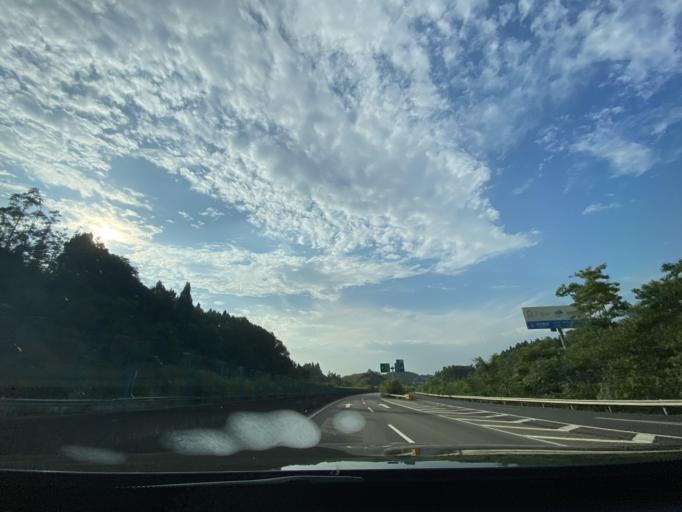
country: CN
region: Sichuan
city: Jiancheng
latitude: 30.2787
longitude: 104.5914
